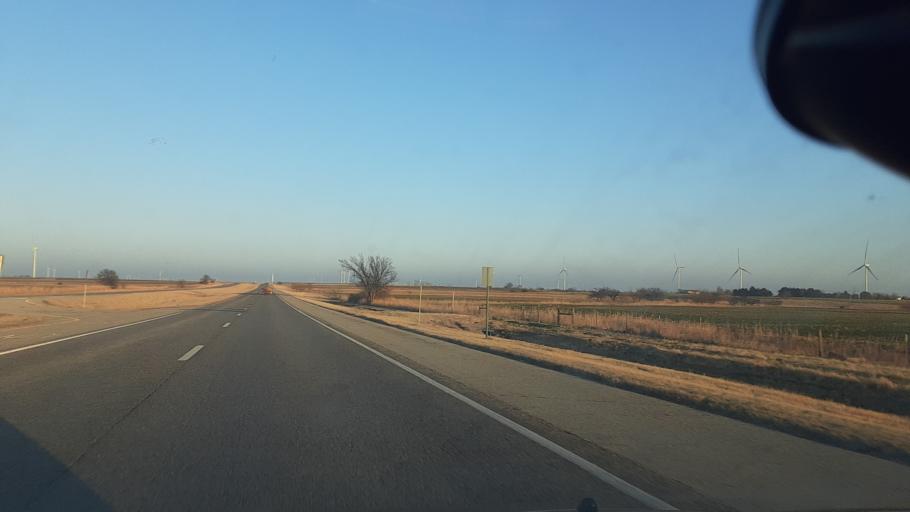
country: US
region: Oklahoma
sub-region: Noble County
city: Perry
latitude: 36.3975
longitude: -97.5064
